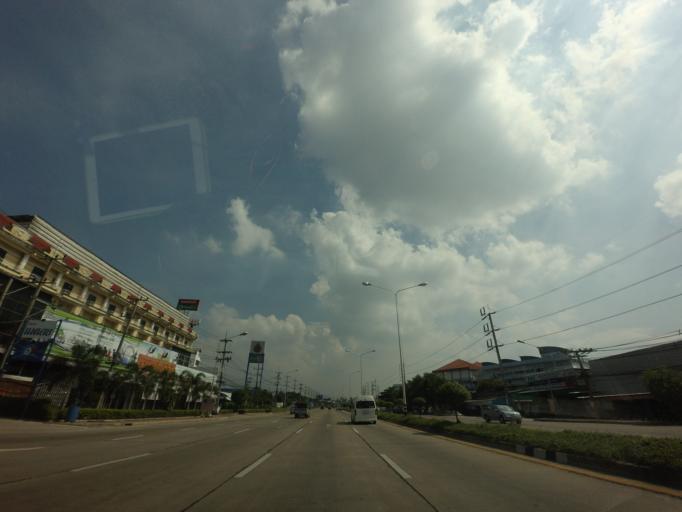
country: TH
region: Nakhon Pathom
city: Sam Phran
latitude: 13.7431
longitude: 100.2356
